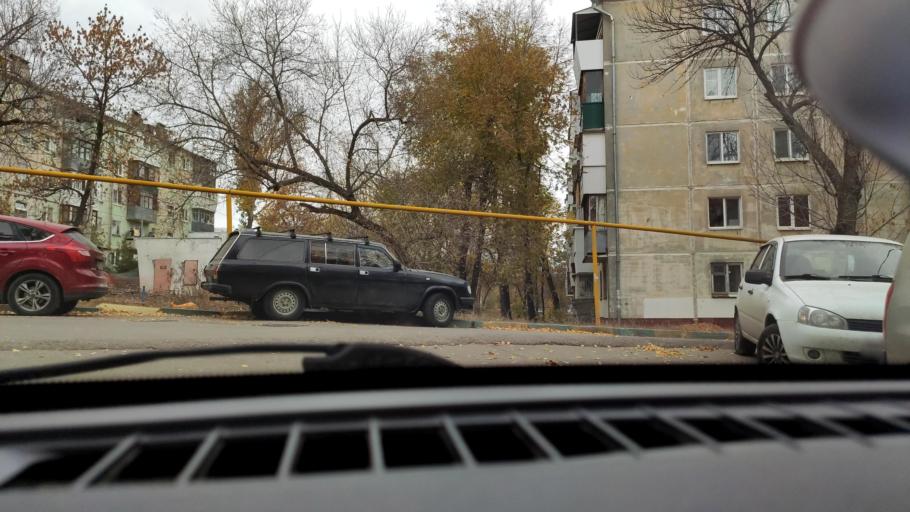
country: RU
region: Samara
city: Samara
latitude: 53.1907
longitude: 50.1943
